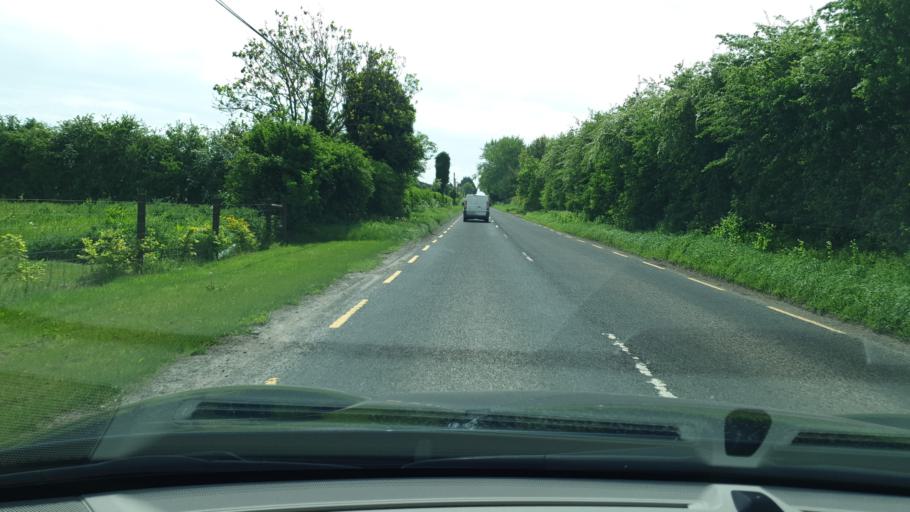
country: IE
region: Leinster
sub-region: An Mhi
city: Navan
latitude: 53.7836
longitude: -6.7308
